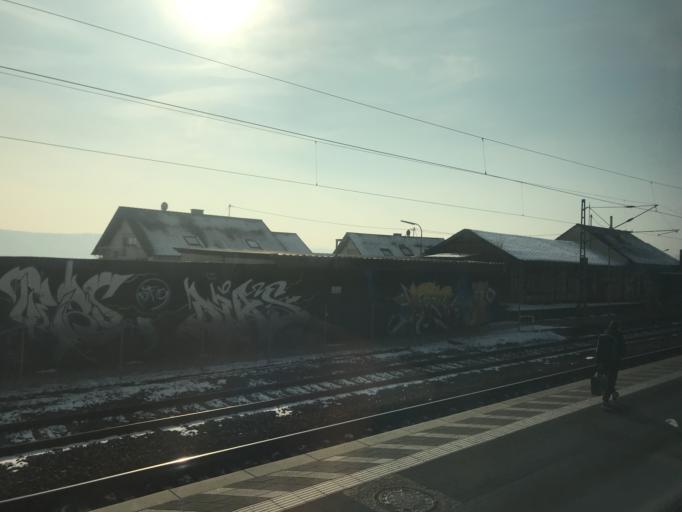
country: DE
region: Rheinland-Pfalz
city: Schweich
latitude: 49.8312
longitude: 6.7412
